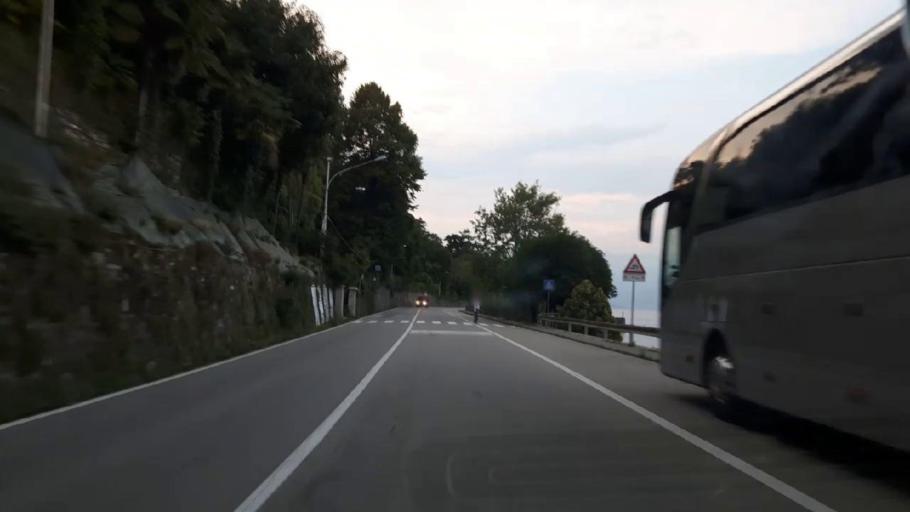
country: IT
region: Piedmont
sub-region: Provincia Verbano-Cusio-Ossola
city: Belgirate
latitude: 45.8430
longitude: 8.5731
